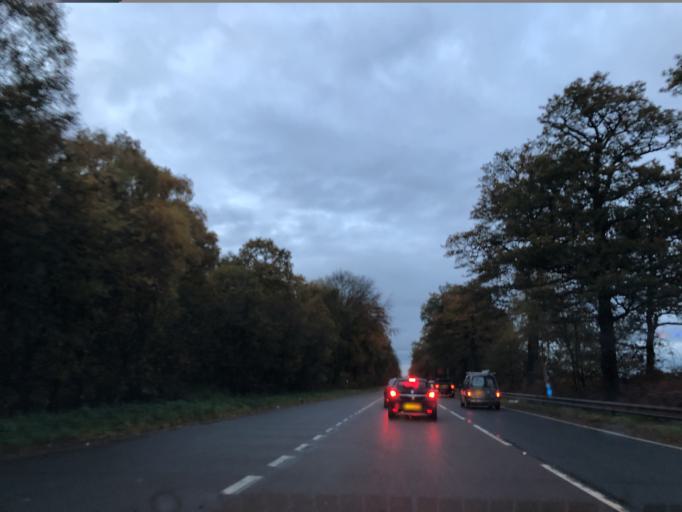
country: GB
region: England
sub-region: Solihull
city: Chelmsley Wood
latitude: 52.4690
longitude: -1.7055
